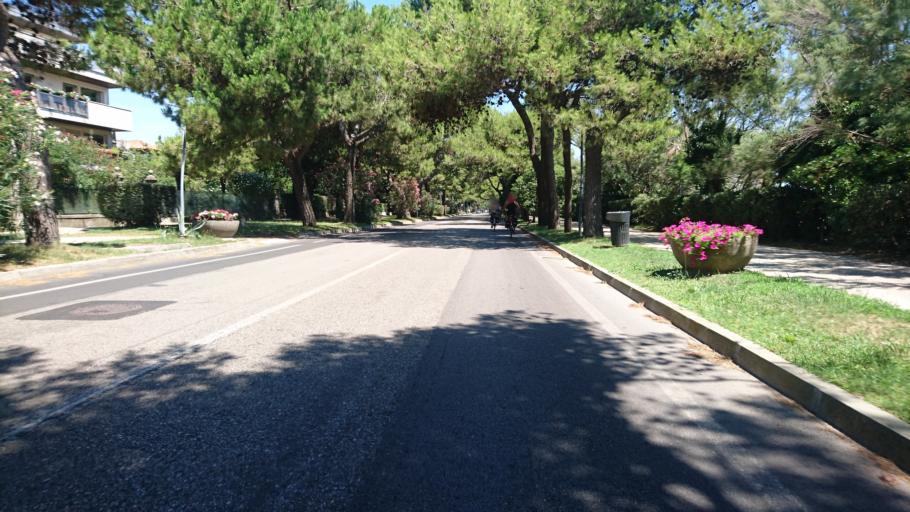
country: IT
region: Veneto
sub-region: Provincia di Venezia
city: Lido
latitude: 45.4087
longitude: 12.3712
